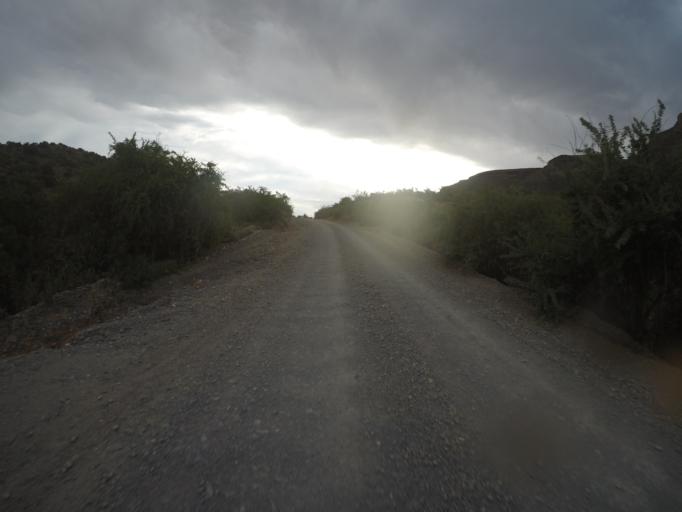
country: ZA
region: Eastern Cape
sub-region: Cacadu District Municipality
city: Willowmore
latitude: -33.5177
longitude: 23.8281
